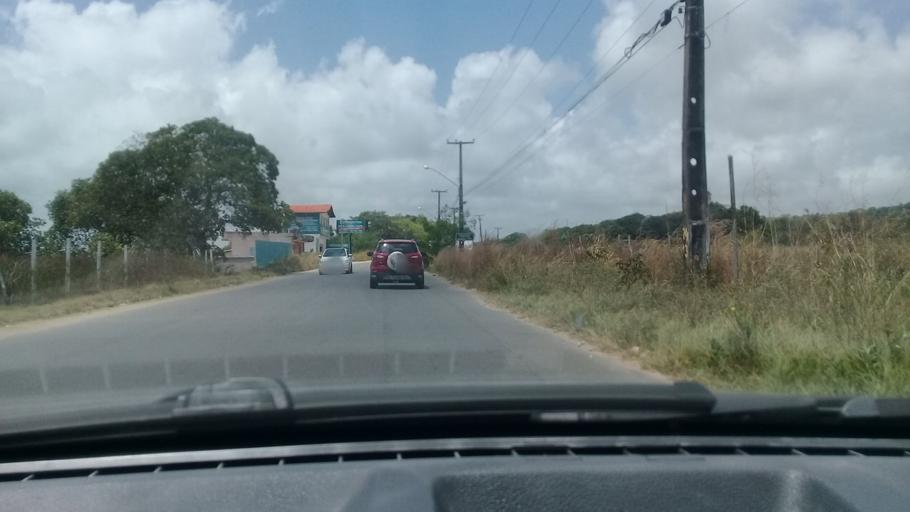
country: BR
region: Pernambuco
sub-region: Itamaraca
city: Itamaraca
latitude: -7.7809
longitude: -34.8366
